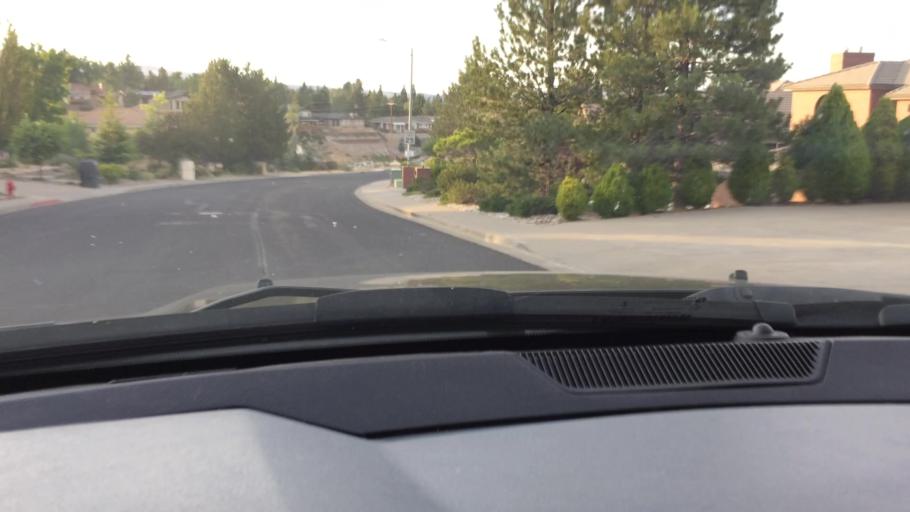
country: US
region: Nevada
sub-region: Washoe County
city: Reno
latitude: 39.4838
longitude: -119.8272
